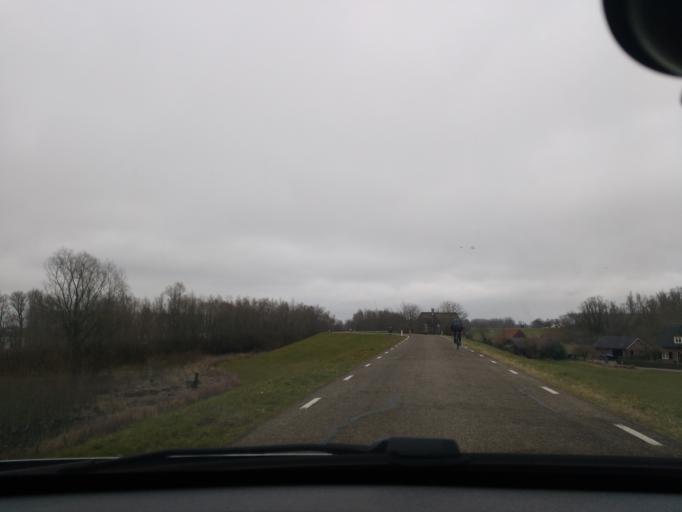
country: NL
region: Gelderland
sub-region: Gemeente Groesbeek
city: Berg en Dal
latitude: 51.8679
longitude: 5.9197
